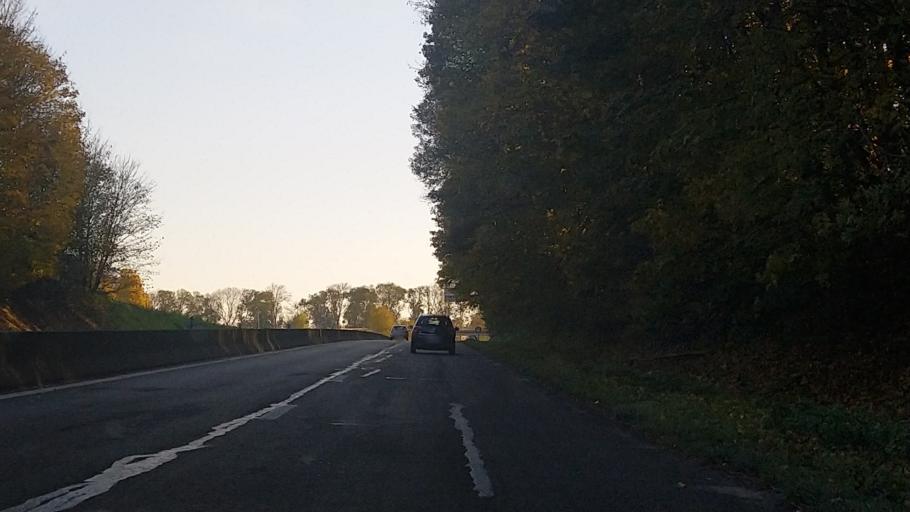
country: FR
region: Ile-de-France
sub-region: Departement du Val-d'Oise
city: Ezanville
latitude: 49.0234
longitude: 2.3497
